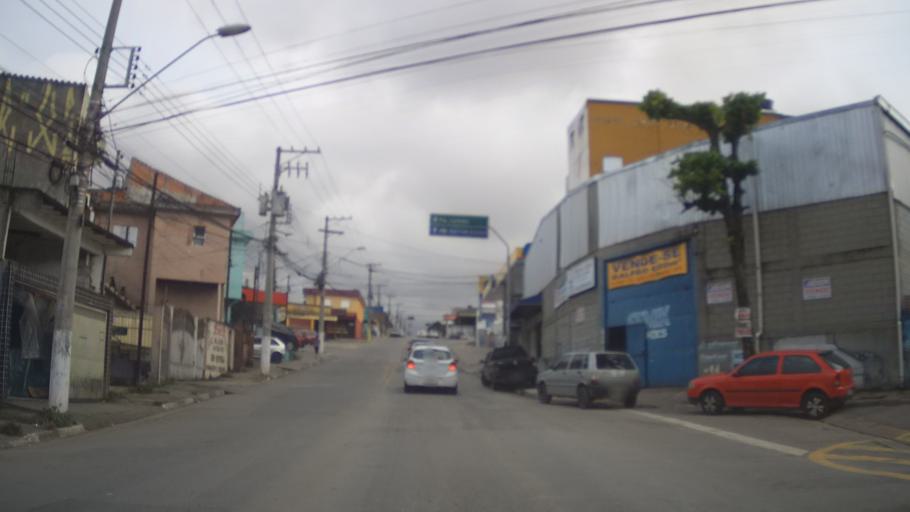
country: BR
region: Sao Paulo
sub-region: Itaquaquecetuba
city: Itaquaquecetuba
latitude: -23.4395
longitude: -46.4283
